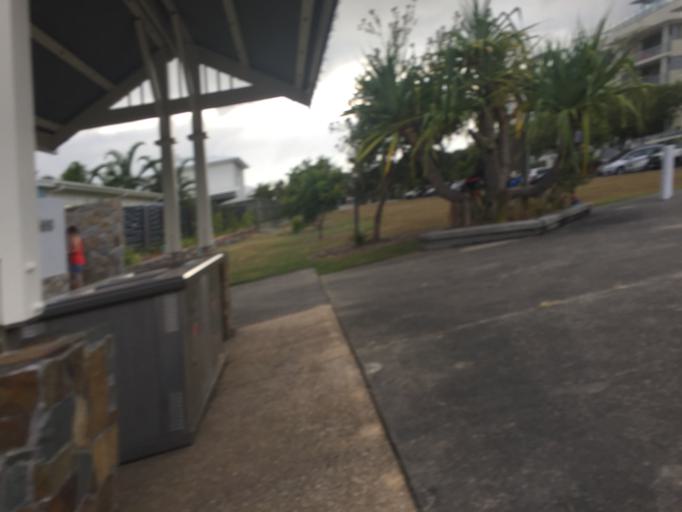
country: AU
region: Queensland
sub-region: Sunshine Coast
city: Coolum Beach
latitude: -26.5746
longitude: 153.0952
